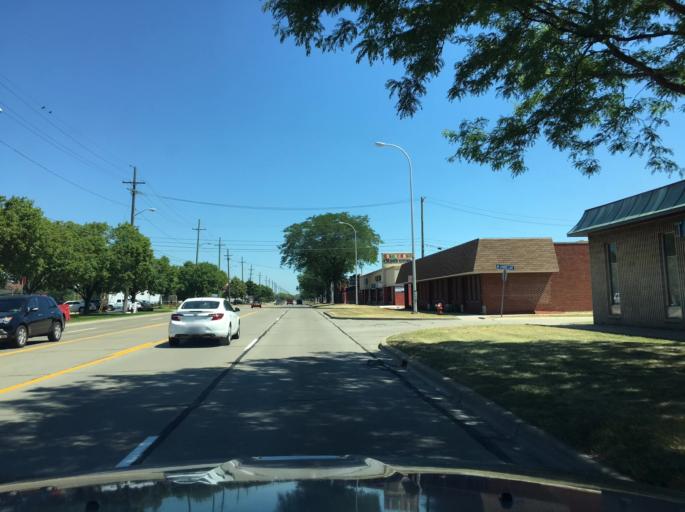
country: US
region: Michigan
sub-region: Wayne County
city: Grosse Pointe Woods
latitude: 42.4709
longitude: -82.9056
